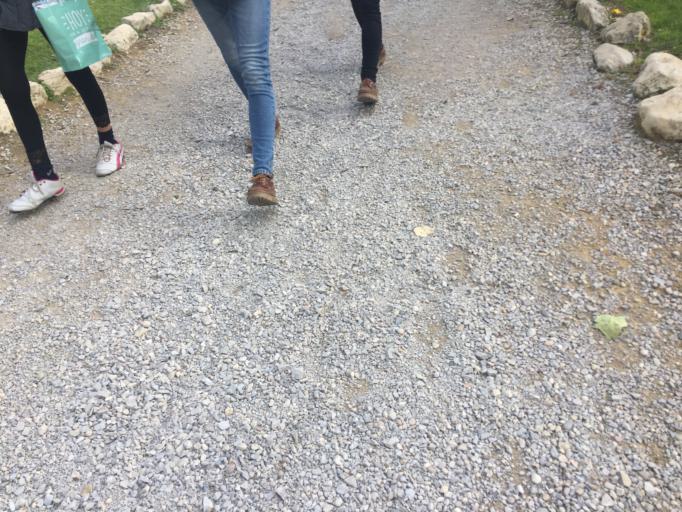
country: ES
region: Andalusia
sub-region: Provincia de Jaen
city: Jaen
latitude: 37.7805
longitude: -3.7909
